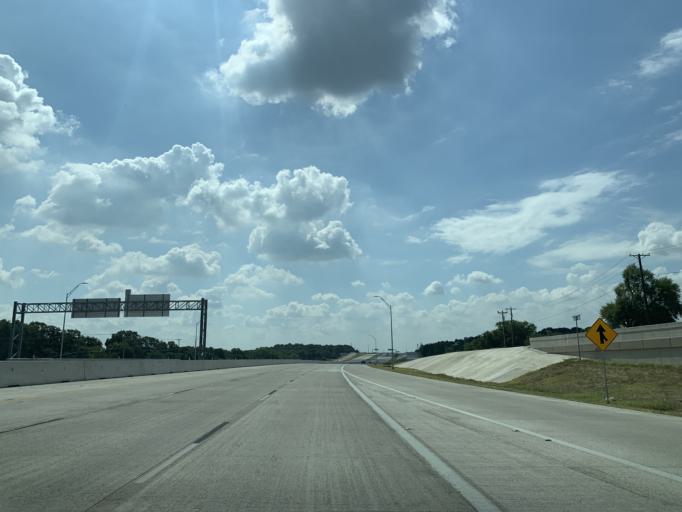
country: US
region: Texas
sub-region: Tarrant County
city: Lakeside
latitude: 32.8524
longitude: -97.5078
